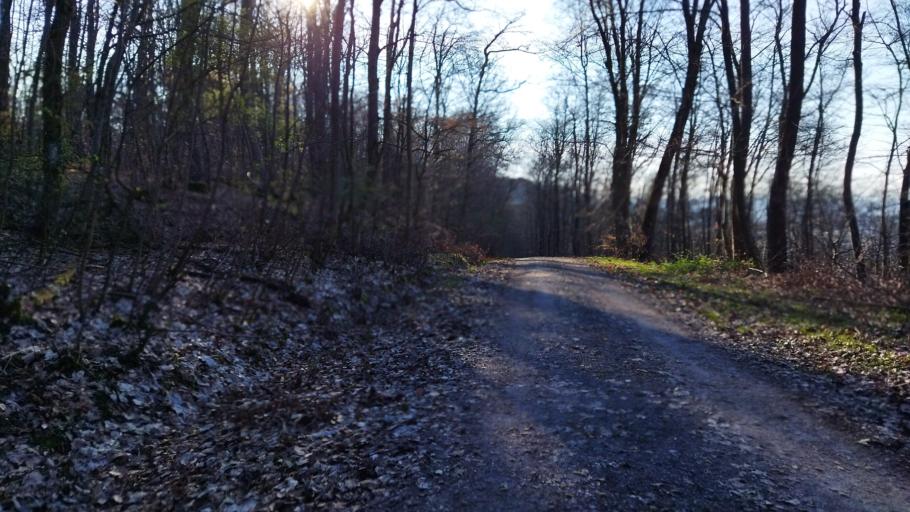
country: DE
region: Baden-Wuerttemberg
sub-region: Karlsruhe Region
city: Sternenfels
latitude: 49.0470
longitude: 8.8658
